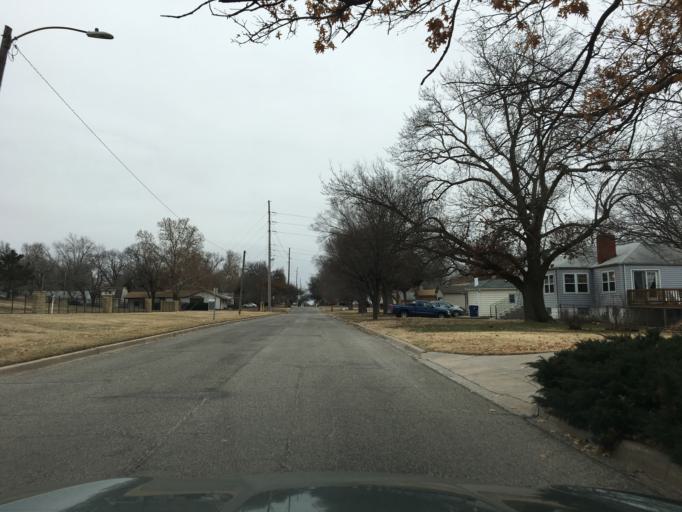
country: US
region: Kansas
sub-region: Sedgwick County
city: Wichita
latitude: 37.6713
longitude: -97.2943
